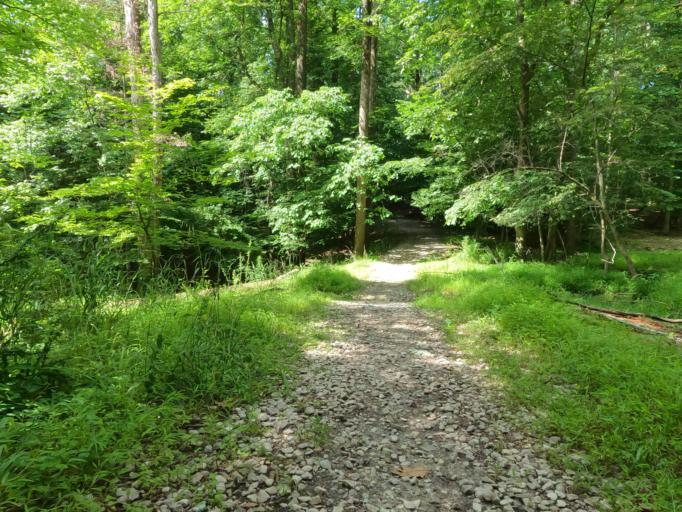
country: US
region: Maryland
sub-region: Howard County
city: Ellicott City
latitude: 39.2846
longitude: -76.7909
